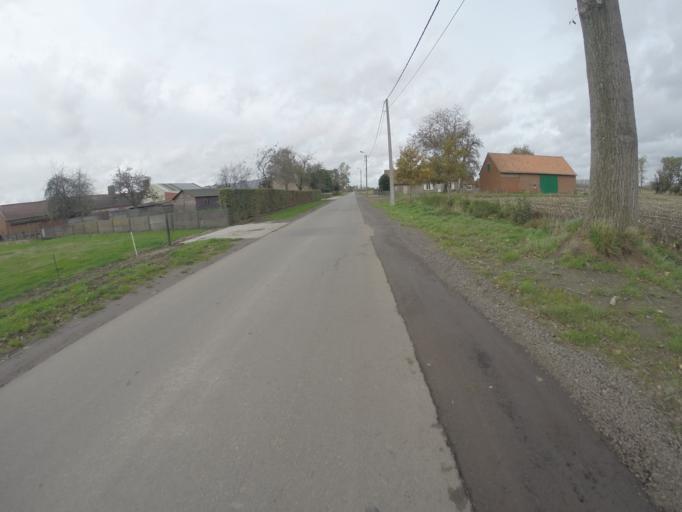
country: BE
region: Flanders
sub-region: Provincie Oost-Vlaanderen
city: Knesselare
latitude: 51.1571
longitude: 3.4022
